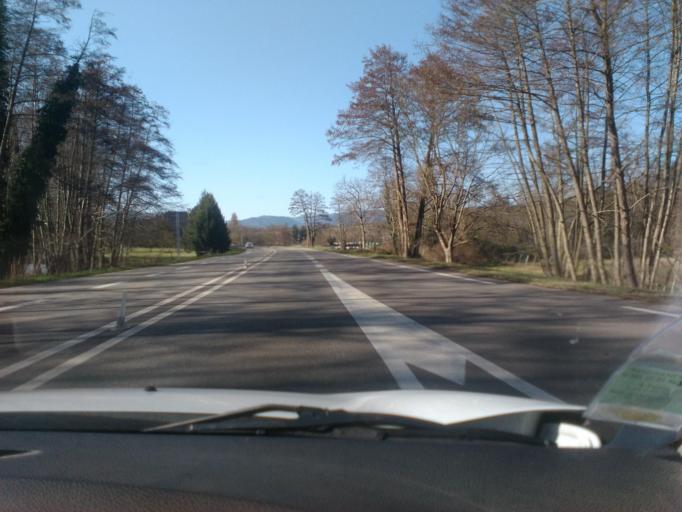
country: FR
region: Alsace
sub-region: Departement du Bas-Rhin
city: Gresswiller
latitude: 48.5383
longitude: 7.4354
